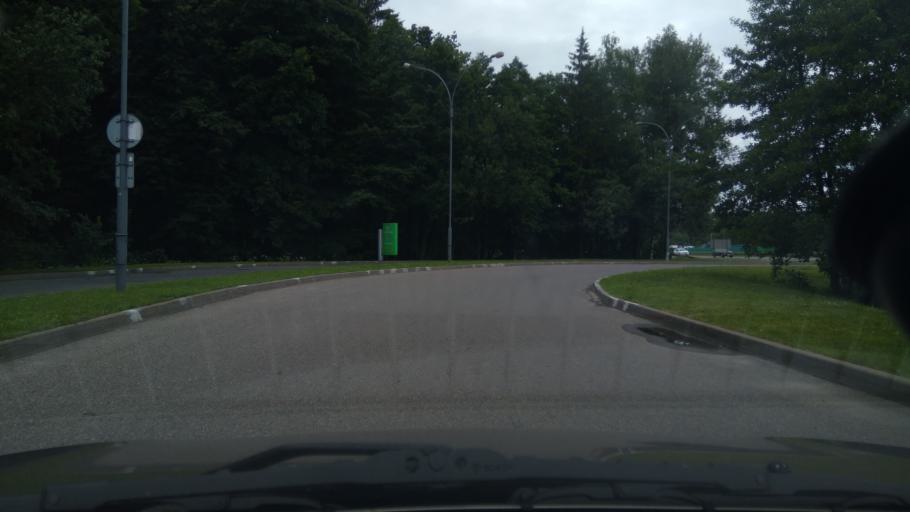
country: BY
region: Minsk
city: Zhdanovichy
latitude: 53.9108
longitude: 27.4015
